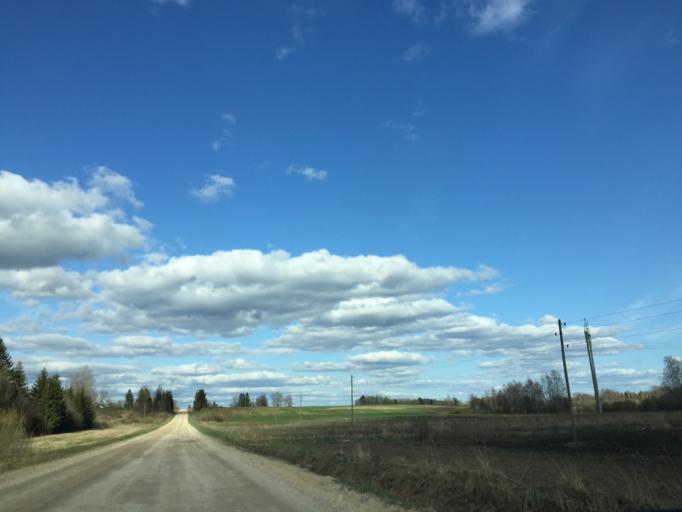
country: LV
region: Rezekne
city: Rezekne
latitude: 56.6446
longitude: 27.3339
